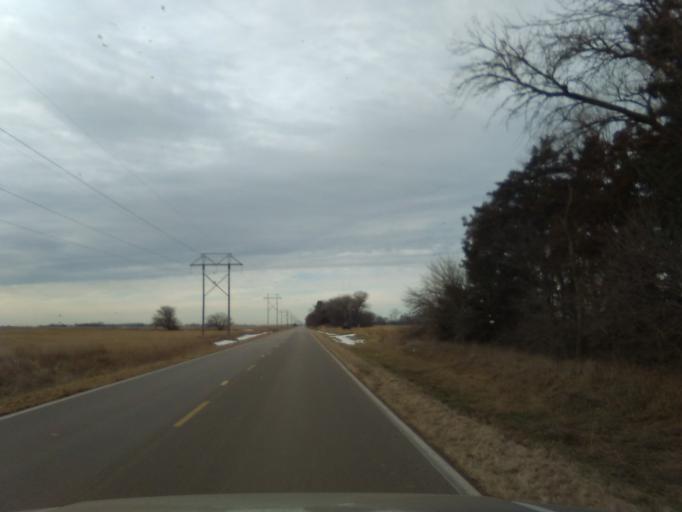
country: US
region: Nebraska
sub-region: Buffalo County
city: Gibbon
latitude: 40.6550
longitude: -98.8069
